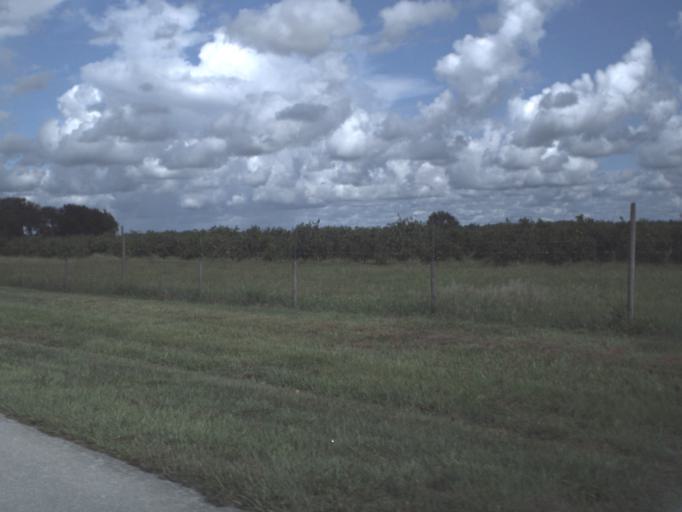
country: US
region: Florida
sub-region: DeSoto County
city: Arcadia
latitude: 27.2628
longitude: -81.9859
